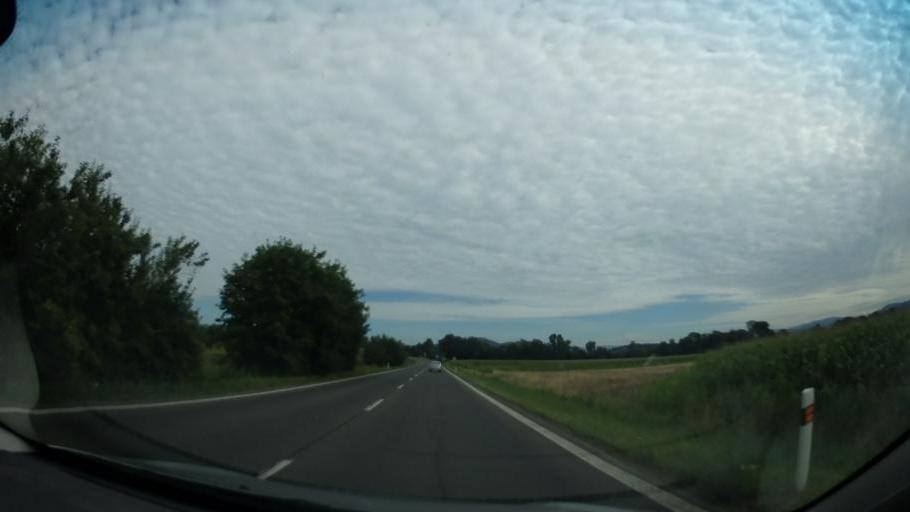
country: CZ
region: Olomoucky
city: Postrelmov
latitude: 49.9136
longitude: 16.9173
